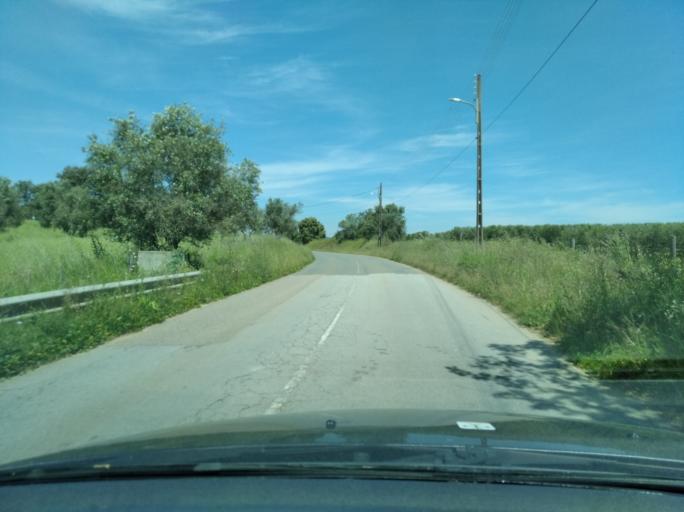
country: PT
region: Portalegre
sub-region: Avis
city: Avis
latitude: 39.0956
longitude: -7.8786
